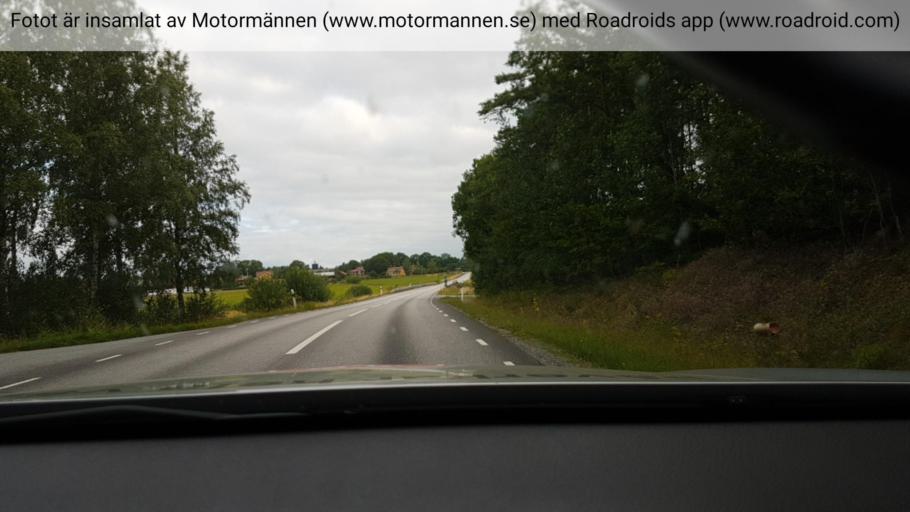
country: SE
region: Stockholm
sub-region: Norrtalje Kommun
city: Skanninge
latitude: 59.8372
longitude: 18.4417
